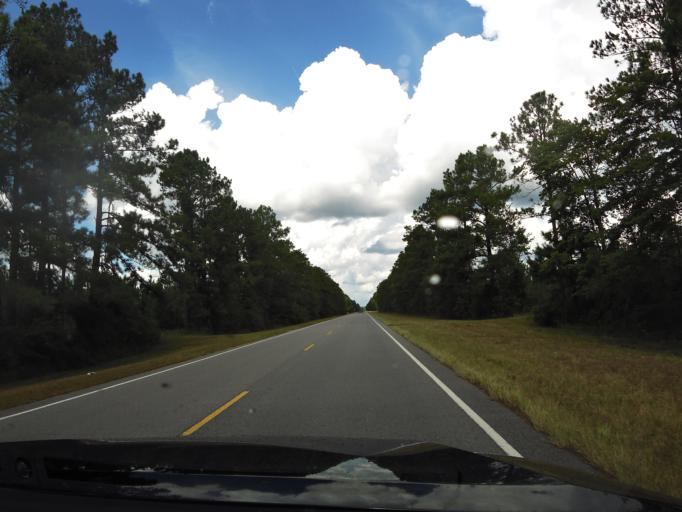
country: US
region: Georgia
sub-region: Charlton County
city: Folkston
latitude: 30.9063
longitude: -82.0181
